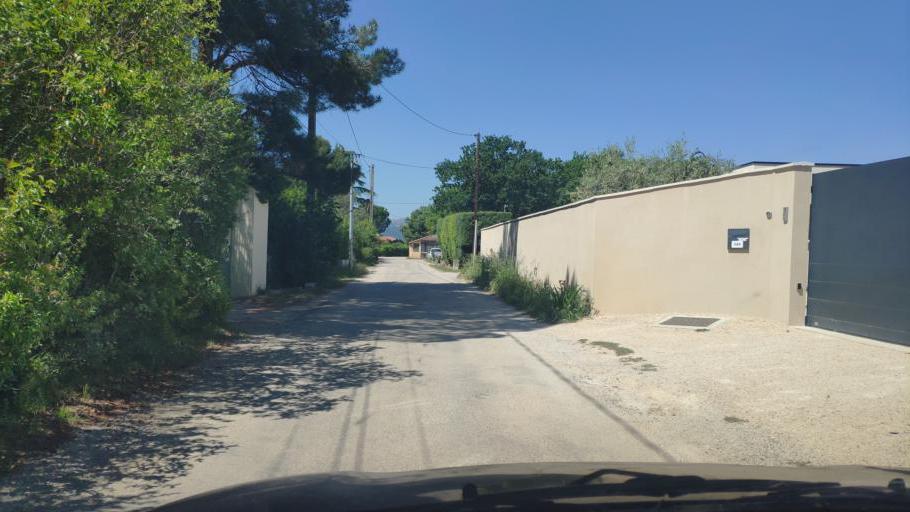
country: FR
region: Provence-Alpes-Cote d'Azur
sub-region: Departement du Vaucluse
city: Carpentras
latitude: 44.0757
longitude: 5.0551
